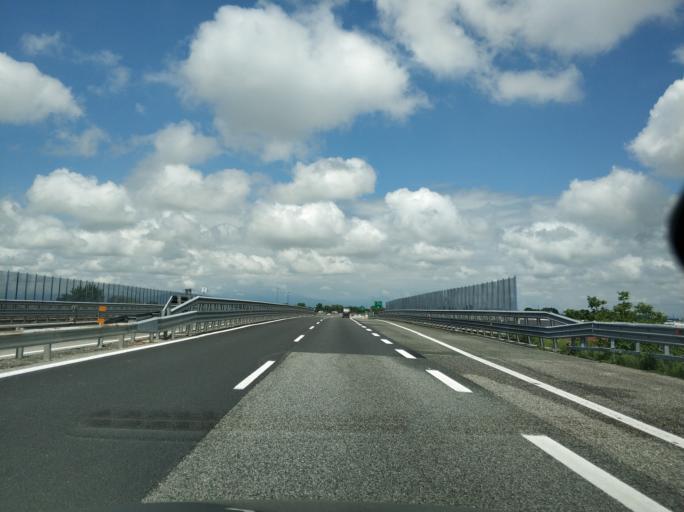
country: IT
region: Piedmont
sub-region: Provincia di Torino
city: Settimo Torinese
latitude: 45.1268
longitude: 7.7313
